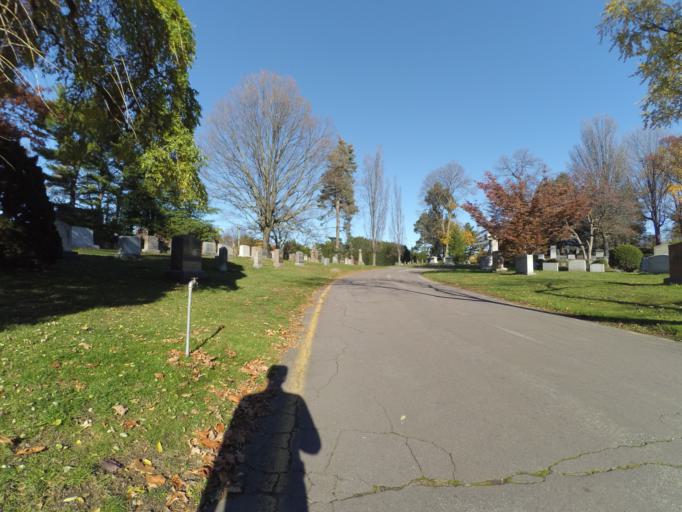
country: US
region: Massachusetts
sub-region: Middlesex County
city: Watertown
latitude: 42.3739
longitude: -71.1498
